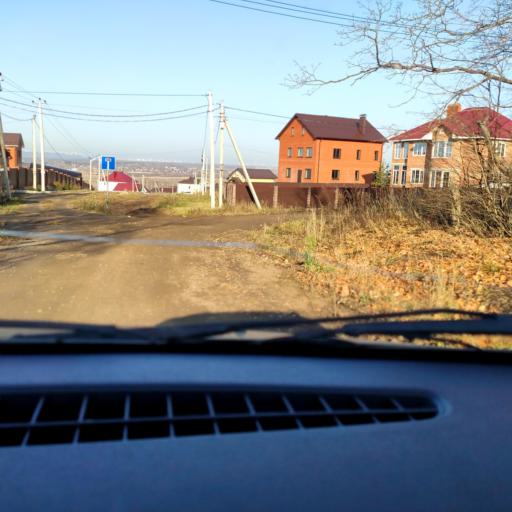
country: RU
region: Bashkortostan
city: Kabakovo
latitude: 54.6303
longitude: 56.0700
